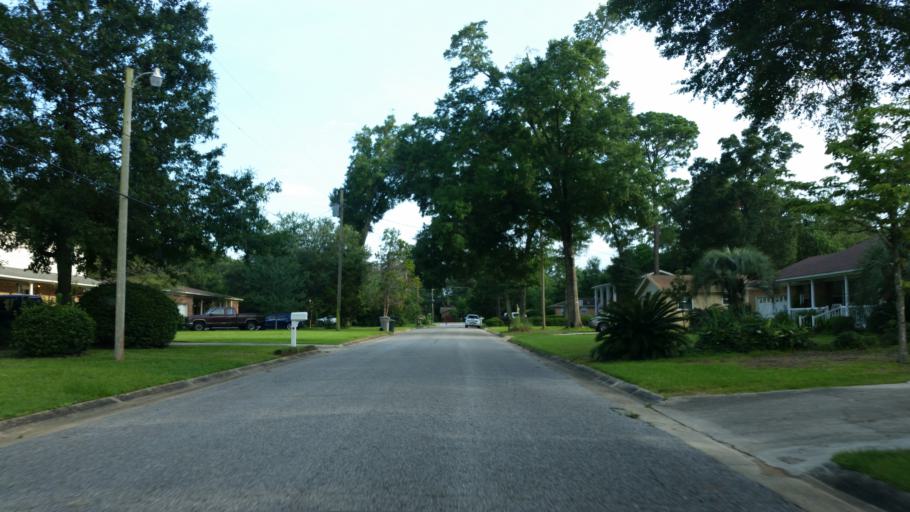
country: US
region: Florida
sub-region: Escambia County
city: Ferry Pass
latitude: 30.5118
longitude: -87.1934
